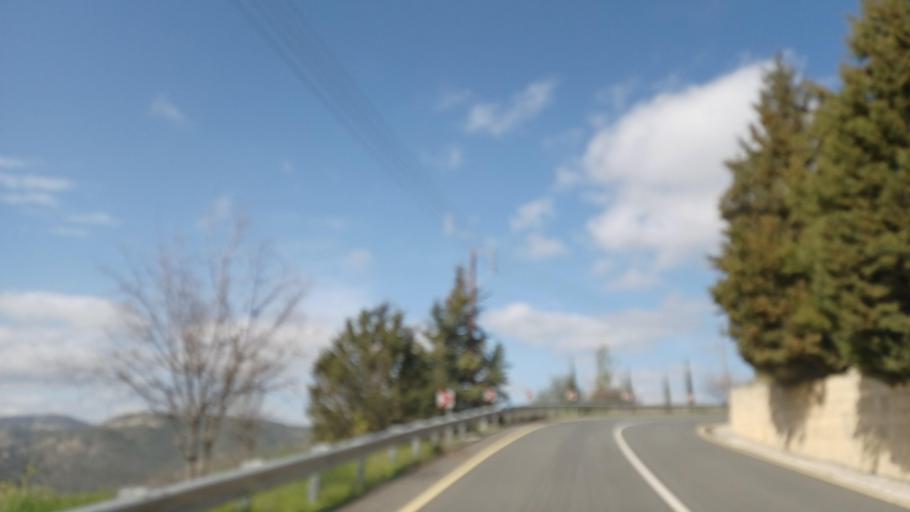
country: CY
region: Limassol
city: Pachna
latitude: 34.8380
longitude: 32.7357
